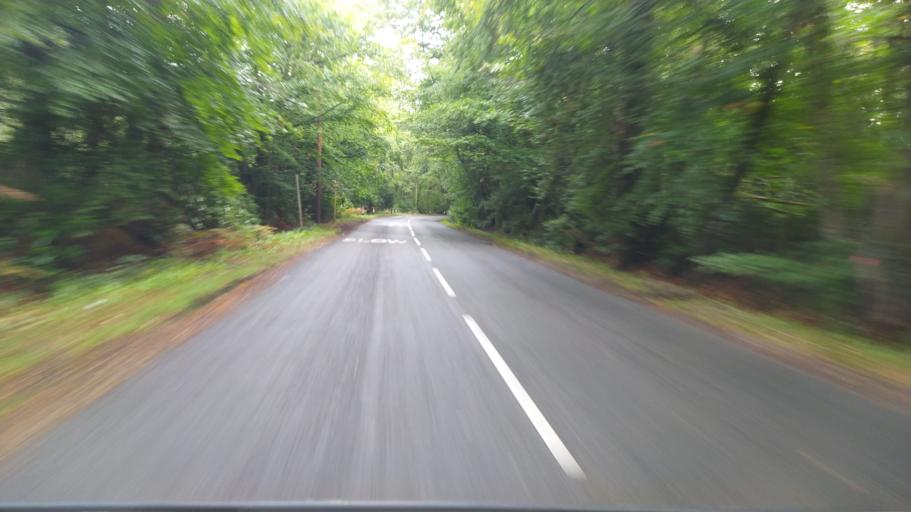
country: GB
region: England
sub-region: Hampshire
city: West Wellow
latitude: 51.0013
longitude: -1.5478
